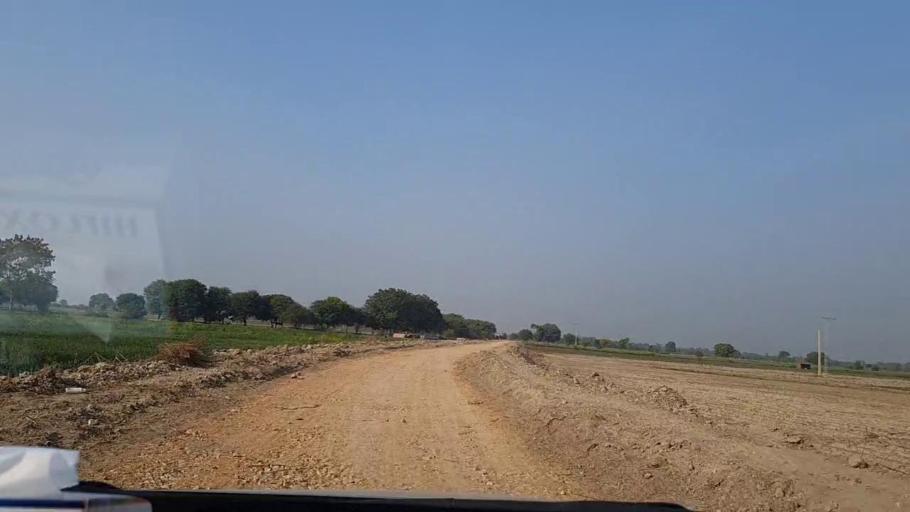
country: PK
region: Sindh
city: Tando Ghulam Ali
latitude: 25.1845
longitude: 68.8745
